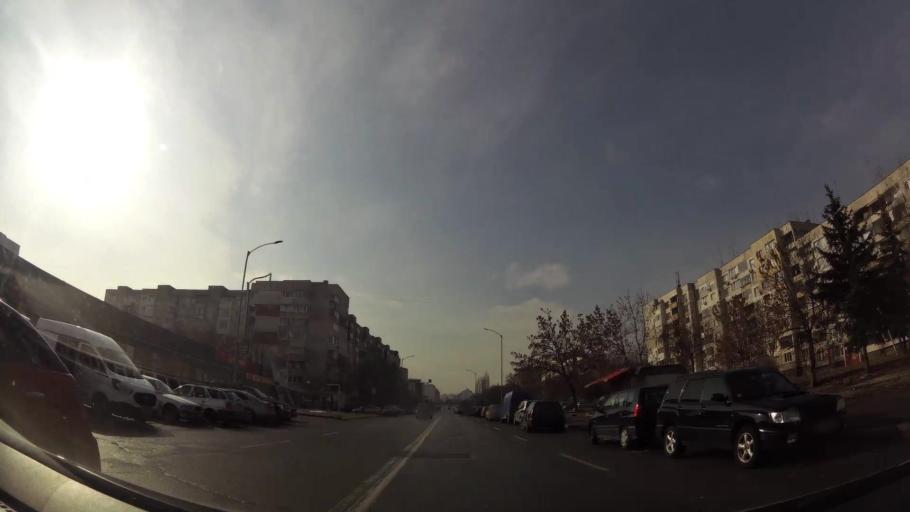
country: BG
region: Sofia-Capital
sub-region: Stolichna Obshtina
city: Sofia
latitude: 42.7198
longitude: 23.2636
